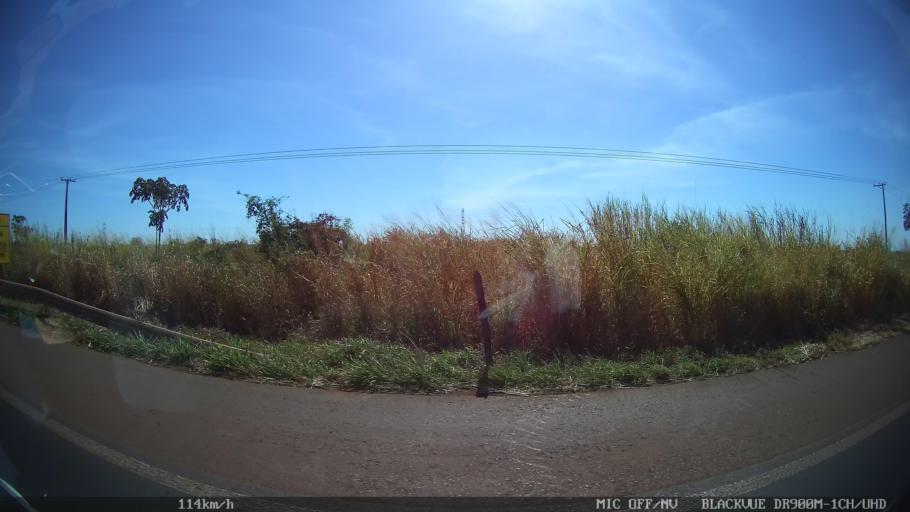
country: BR
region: Sao Paulo
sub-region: Barretos
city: Barretos
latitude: -20.4789
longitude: -48.5005
